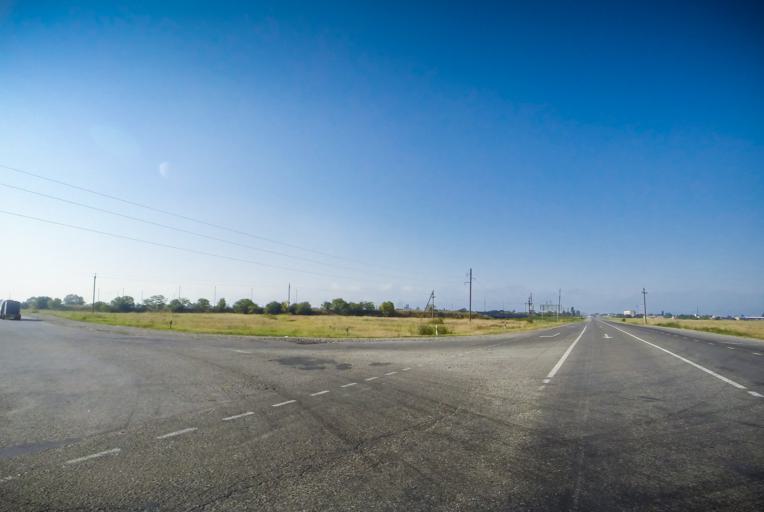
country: RU
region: North Ossetia
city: Ardon
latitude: 43.2044
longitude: 44.2865
